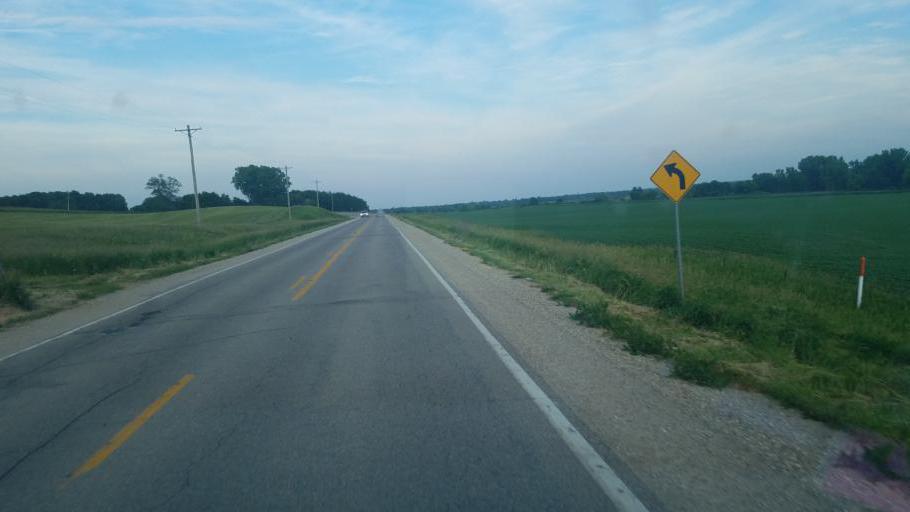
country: US
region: Iowa
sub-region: Benton County
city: Belle Plaine
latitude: 41.9074
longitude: -92.3361
